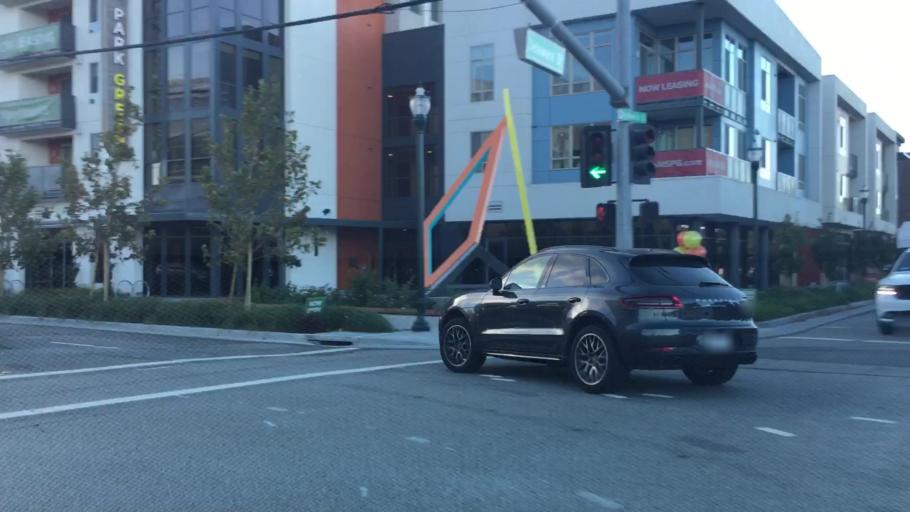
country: US
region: California
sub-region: San Mateo County
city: San Mateo
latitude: 37.5543
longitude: -122.3062
